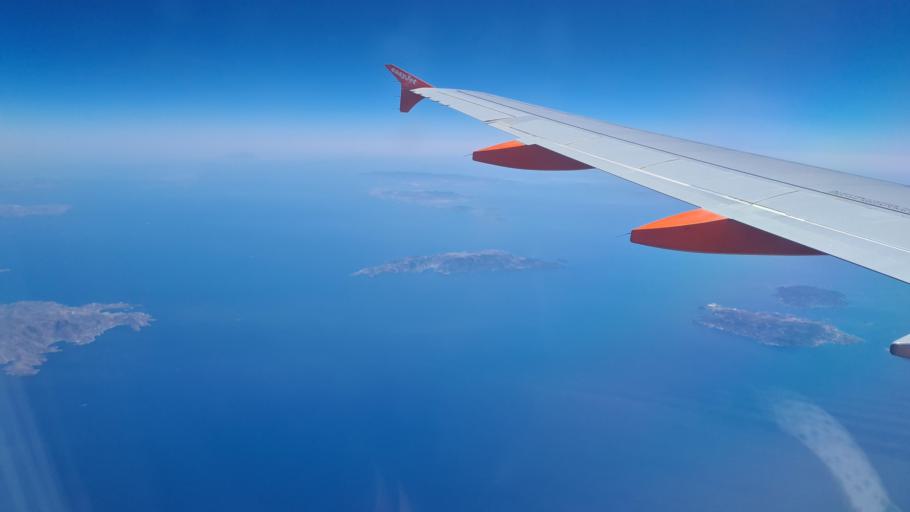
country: GR
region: South Aegean
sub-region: Nomos Kykladon
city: Kythnos
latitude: 37.2535
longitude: 24.0198
